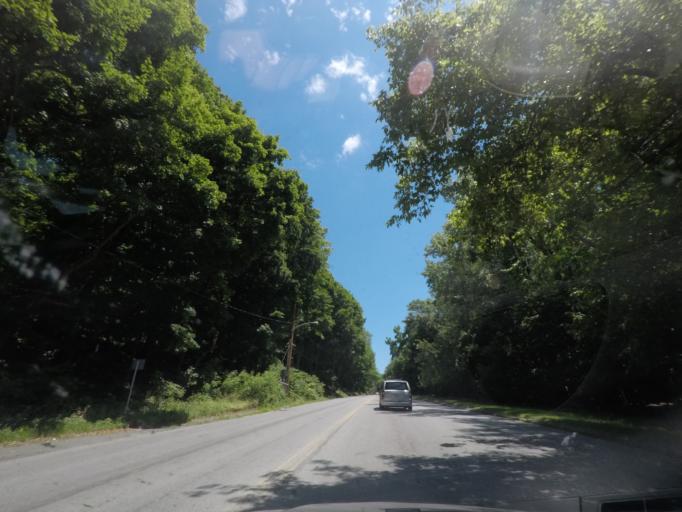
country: US
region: New York
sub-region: Rensselaer County
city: Troy
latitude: 42.7046
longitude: -73.6960
